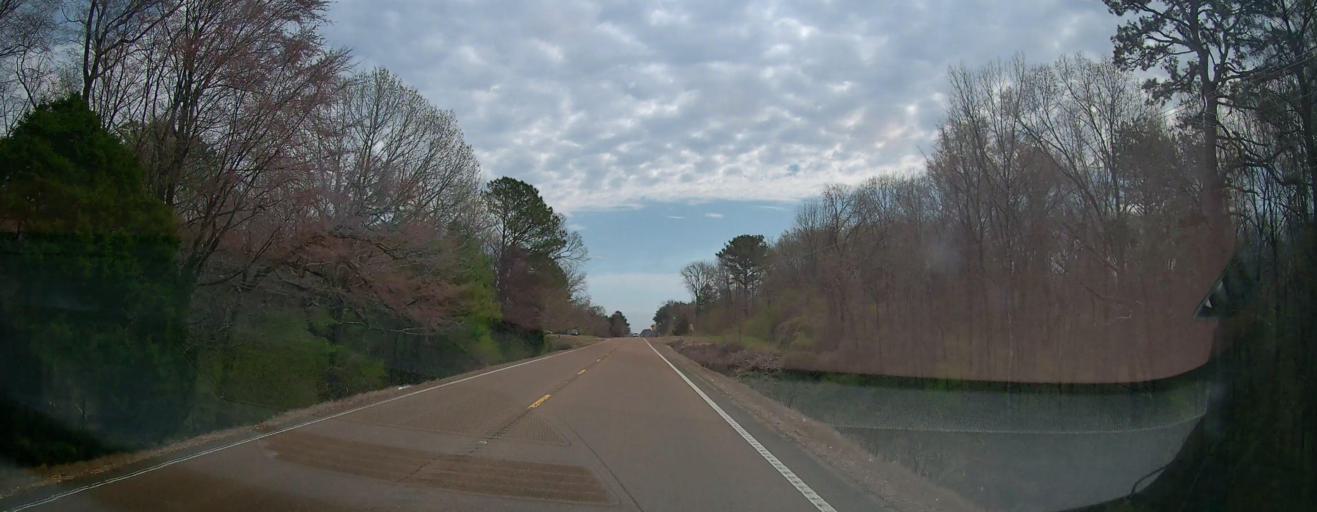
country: US
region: Mississippi
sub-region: Marshall County
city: Holly Springs
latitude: 34.8259
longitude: -89.5580
